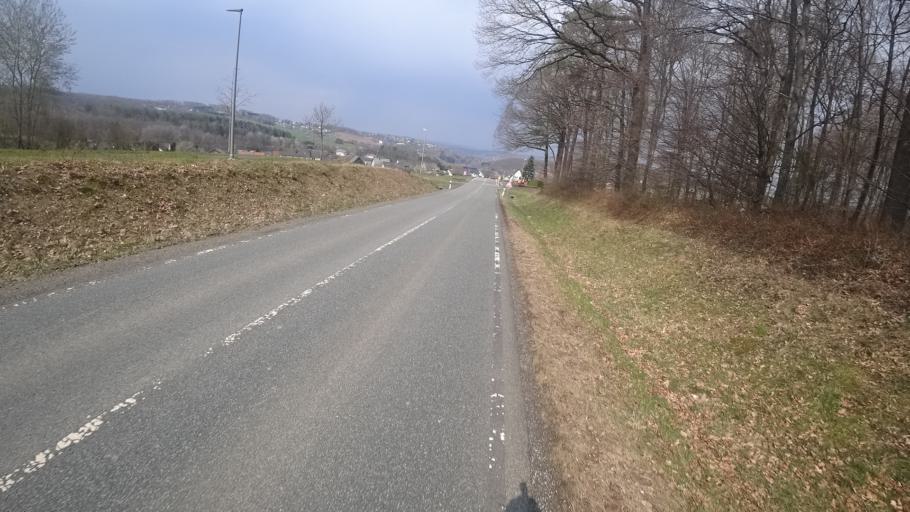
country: DE
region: Rheinland-Pfalz
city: Elben
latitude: 50.7272
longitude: 7.8258
